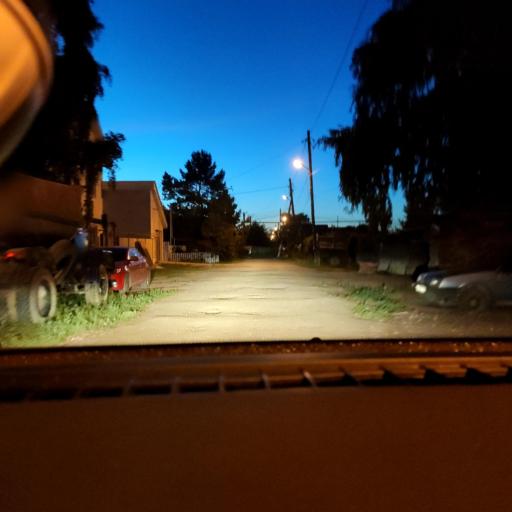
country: RU
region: Samara
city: Samara
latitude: 53.1818
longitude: 50.2336
